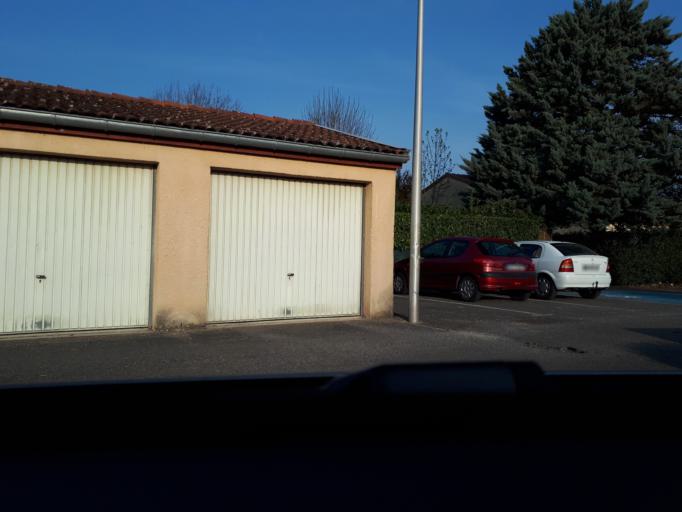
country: FR
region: Rhone-Alpes
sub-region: Departement de l'Isere
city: Bourgoin-Jallieu
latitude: 45.6122
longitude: 5.2675
